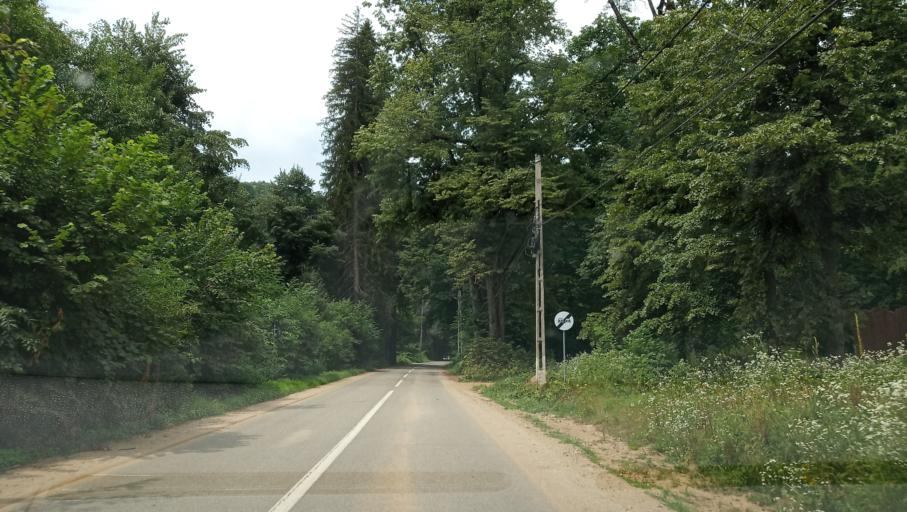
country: RO
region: Gorj
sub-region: Comuna Tismana
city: Pocruia
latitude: 45.0722
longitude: 22.9344
